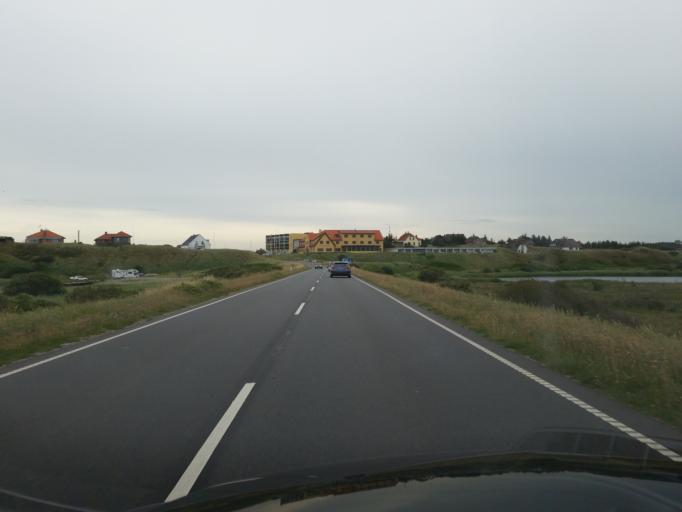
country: DK
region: Central Jutland
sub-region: Ringkobing-Skjern Kommune
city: Hvide Sande
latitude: 55.8179
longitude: 8.1867
